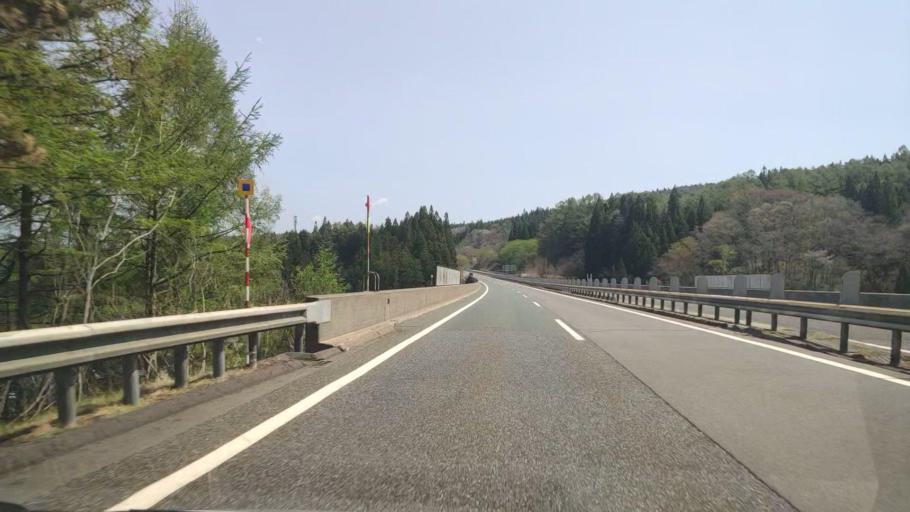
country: JP
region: Iwate
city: Ichinohe
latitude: 40.1794
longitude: 141.1596
